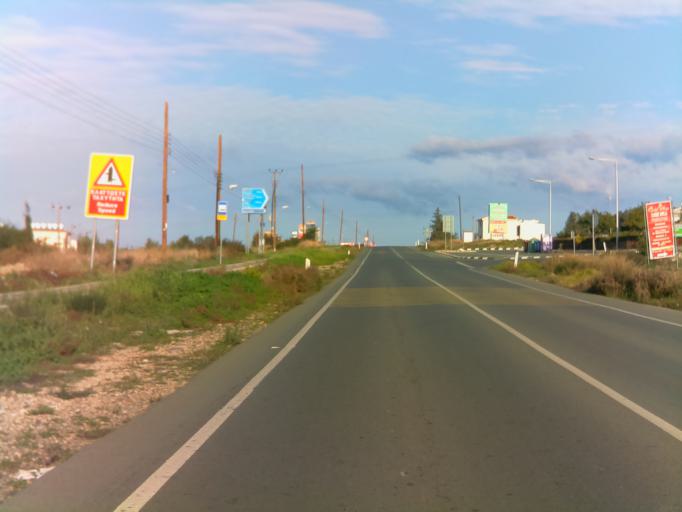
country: CY
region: Pafos
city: Pegeia
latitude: 34.8734
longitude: 32.3588
